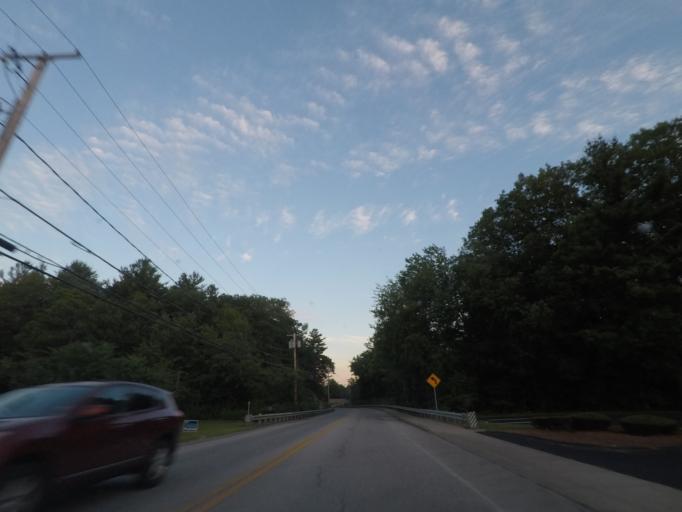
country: US
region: Massachusetts
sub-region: Worcester County
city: Sturbridge
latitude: 42.0906
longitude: -72.0668
